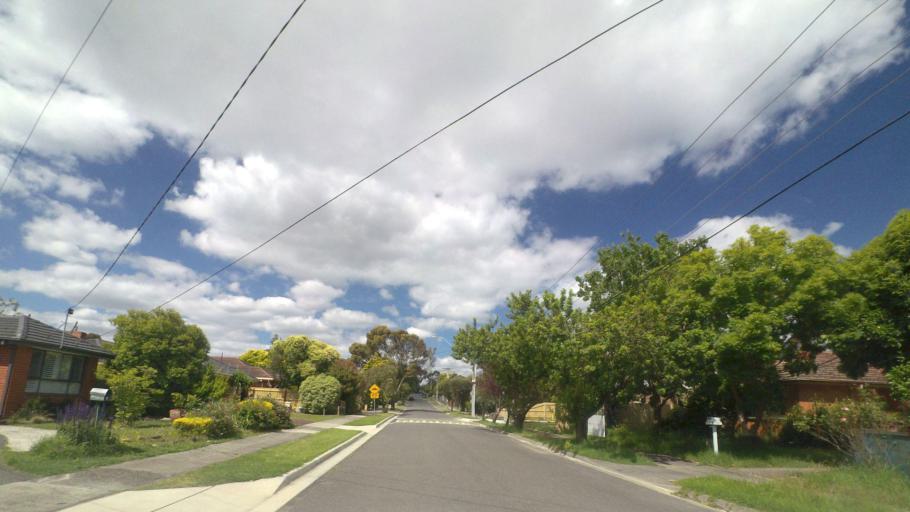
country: AU
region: Victoria
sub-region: Knox
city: Bayswater
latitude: -37.8632
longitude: 145.2494
